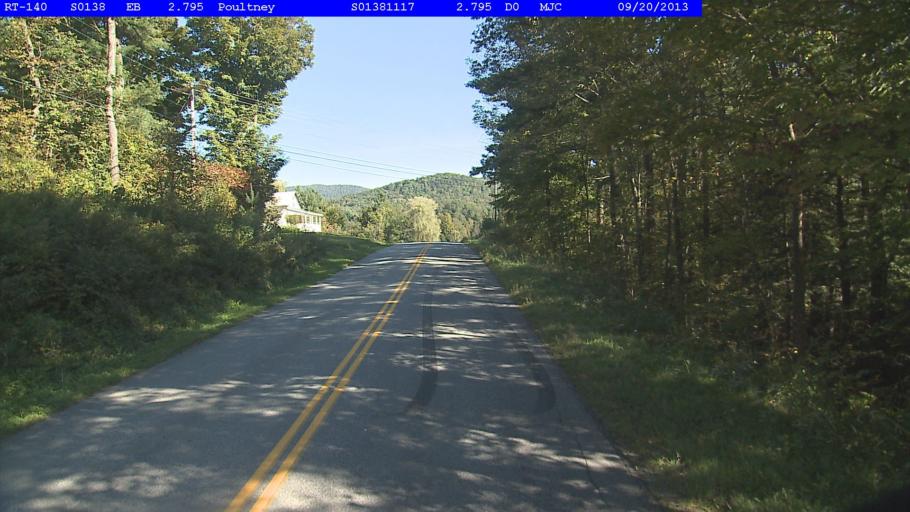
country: US
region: Vermont
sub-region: Rutland County
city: Poultney
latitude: 43.5231
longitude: -73.1839
